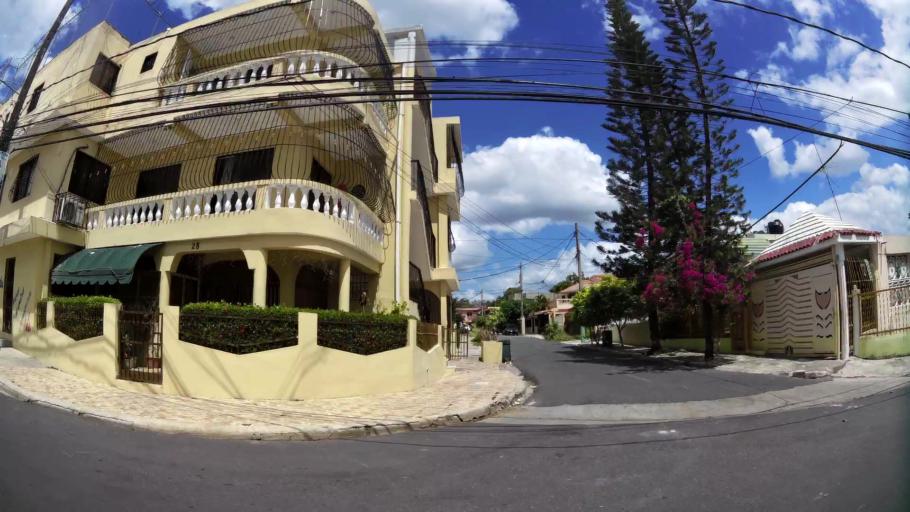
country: DO
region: Nacional
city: Ensanche Luperon
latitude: 18.5218
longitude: -69.9105
